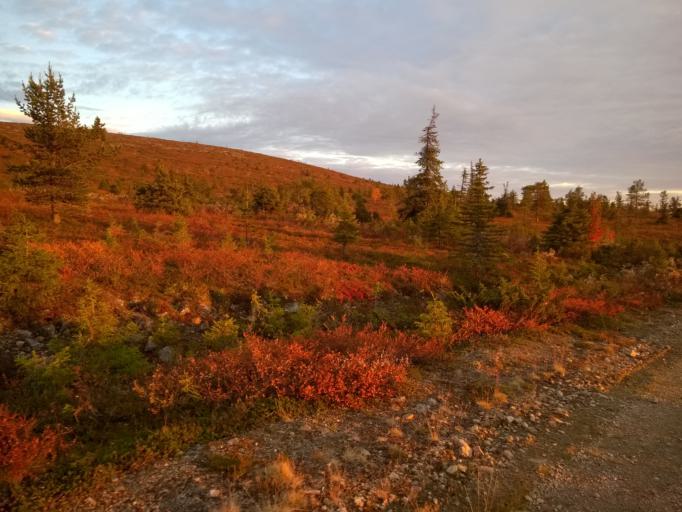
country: FI
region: Lapland
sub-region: Tunturi-Lappi
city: Muonio
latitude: 67.9778
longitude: 24.1041
